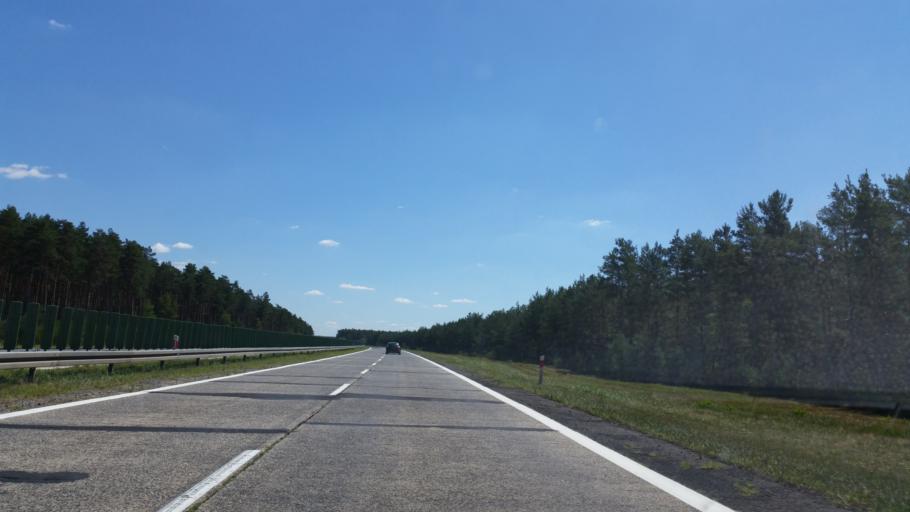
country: PL
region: Lower Silesian Voivodeship
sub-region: Powiat boleslawiecki
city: Boleslawiec
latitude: 51.3717
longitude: 15.5634
